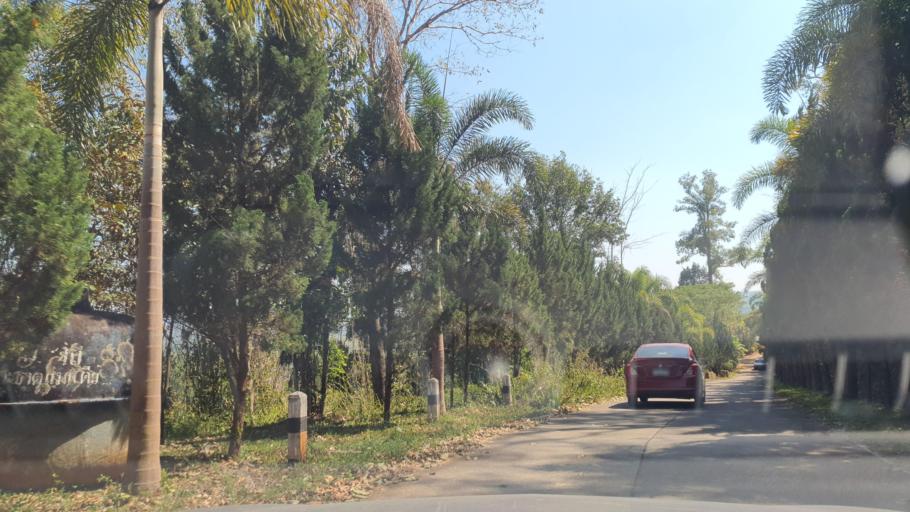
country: TH
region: Lampang
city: Wang Nuea
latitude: 19.1851
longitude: 99.4993
